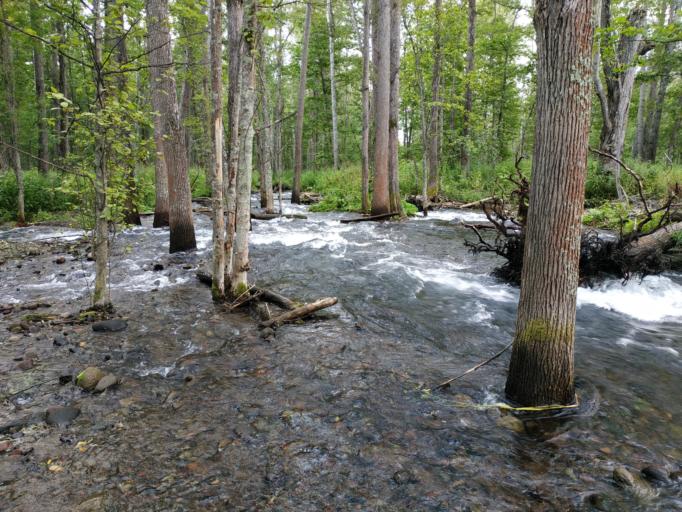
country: RU
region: Kamtsjatka
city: Yelizovo
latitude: 53.8280
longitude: 158.0875
